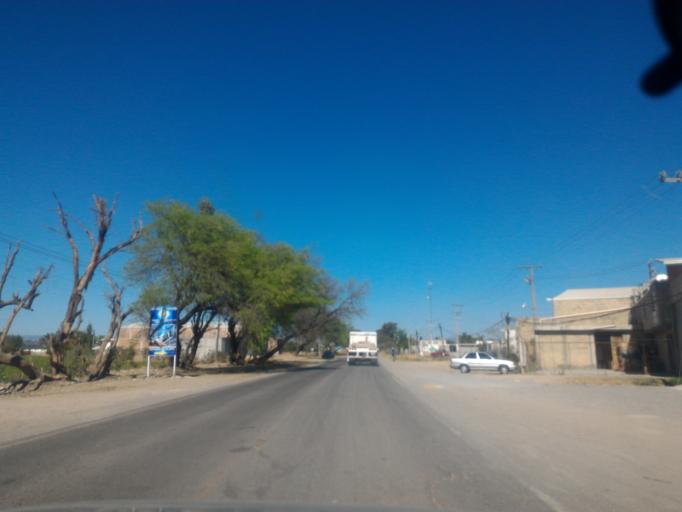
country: MX
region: Guanajuato
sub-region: Leon
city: Malagana (San Antonio del Monte)
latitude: 21.0424
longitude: -101.7650
